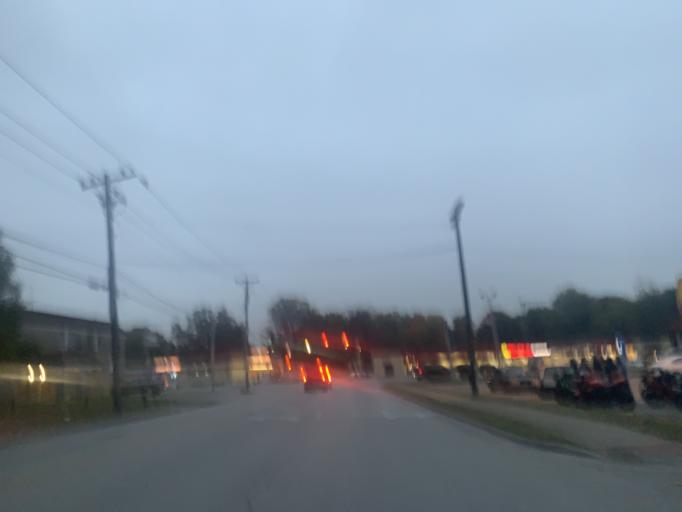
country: US
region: Kentucky
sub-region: Jefferson County
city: Shively
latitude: 38.2148
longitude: -85.7969
